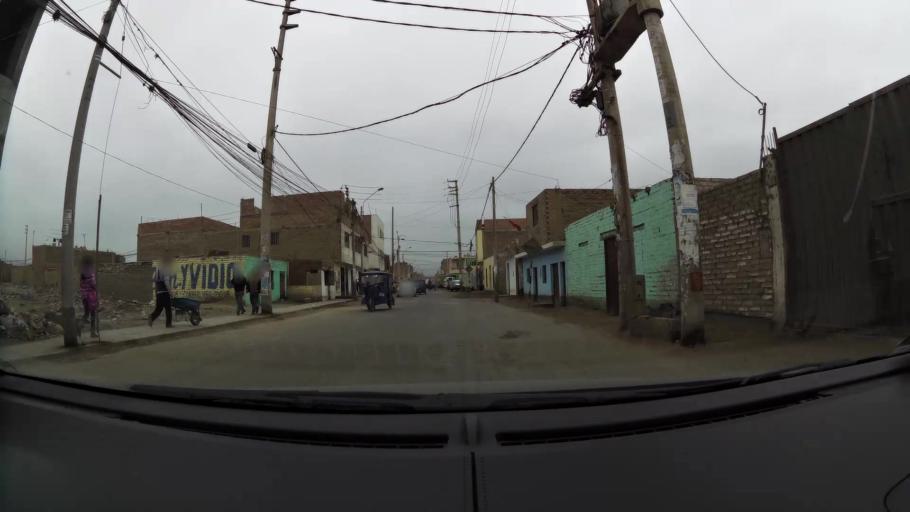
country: PE
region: Lima
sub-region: Barranca
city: Barranca
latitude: -10.7454
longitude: -77.7622
